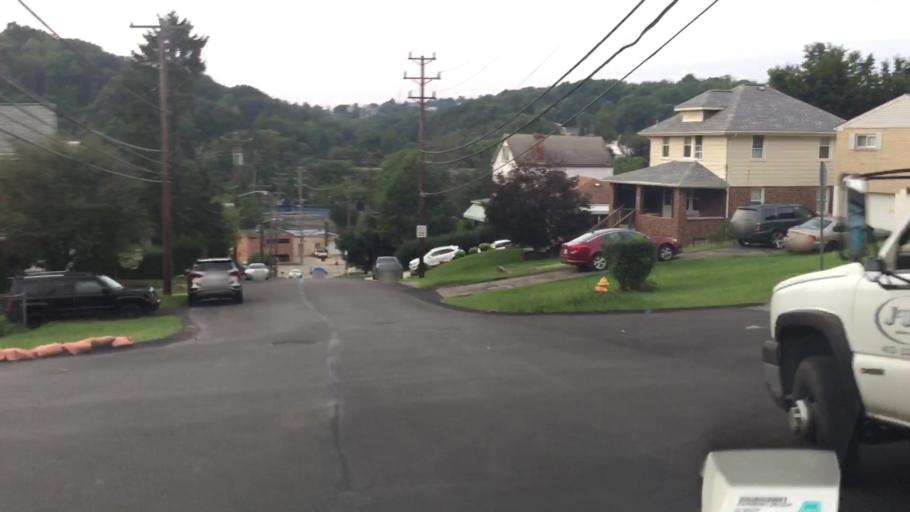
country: US
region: Pennsylvania
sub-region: Allegheny County
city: Whitehall
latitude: 40.3759
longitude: -80.0026
